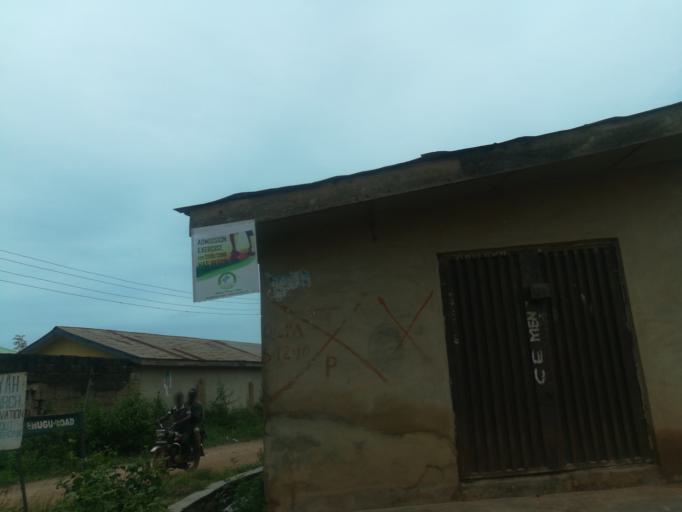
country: NG
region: Oyo
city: Ibadan
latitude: 7.3193
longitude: 3.8836
